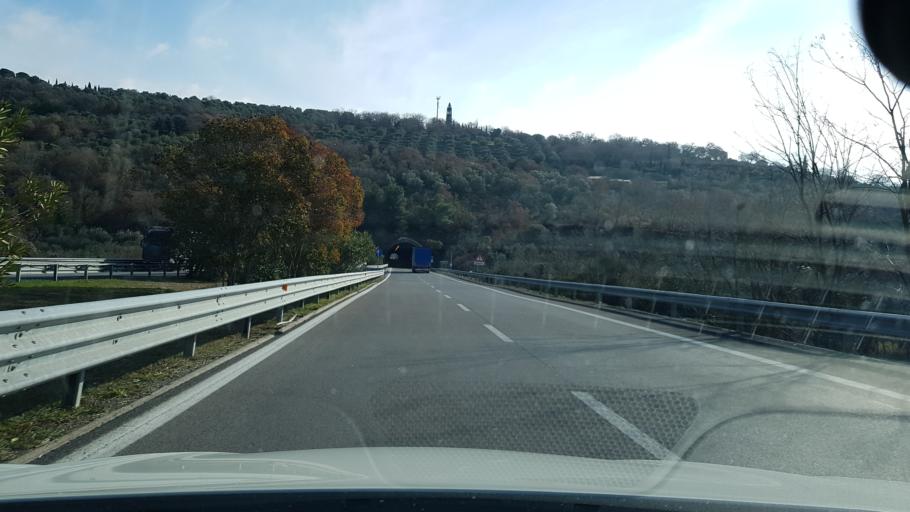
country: IT
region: Umbria
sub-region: Provincia di Perugia
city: Passignano sul Trasimeno
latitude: 43.1925
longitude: 12.1404
